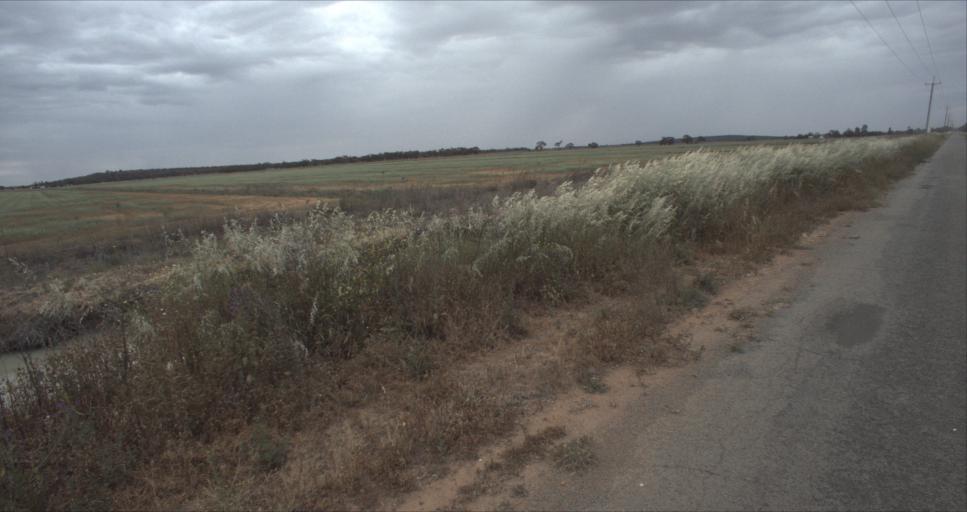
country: AU
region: New South Wales
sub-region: Leeton
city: Leeton
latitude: -34.4321
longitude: 146.3365
